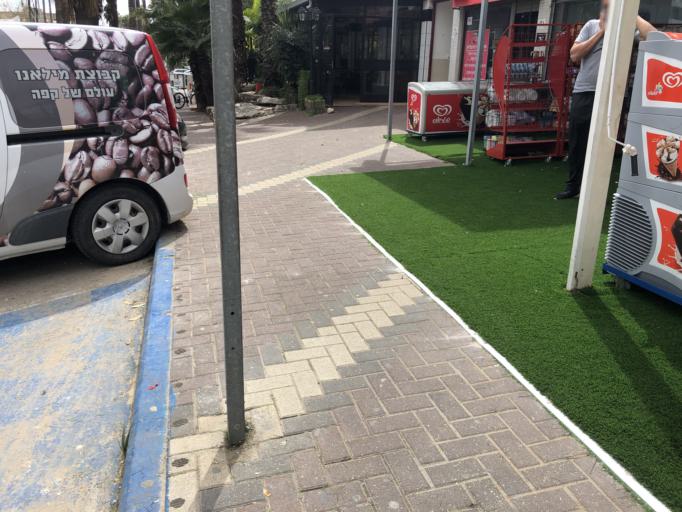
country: IL
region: Haifa
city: Hadera
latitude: 32.4736
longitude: 34.9735
